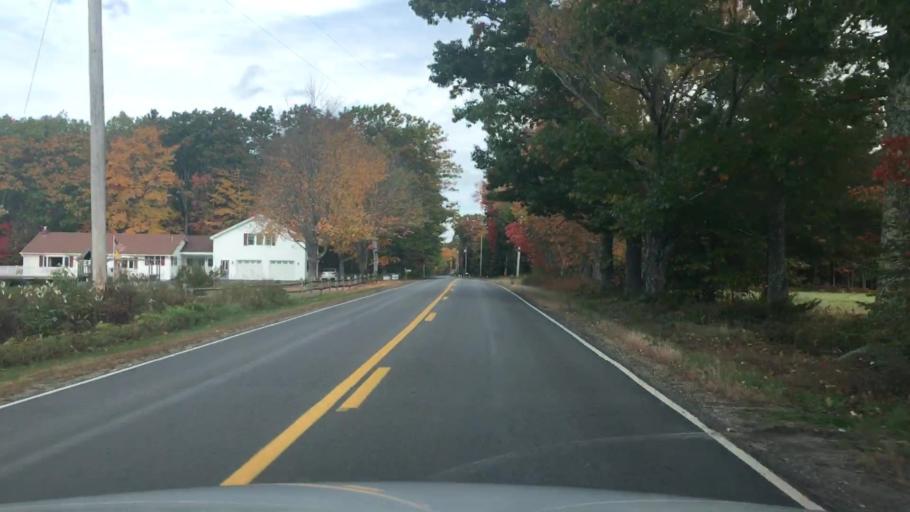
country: US
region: Maine
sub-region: Waldo County
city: Searsmont
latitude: 44.4133
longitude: -69.1376
